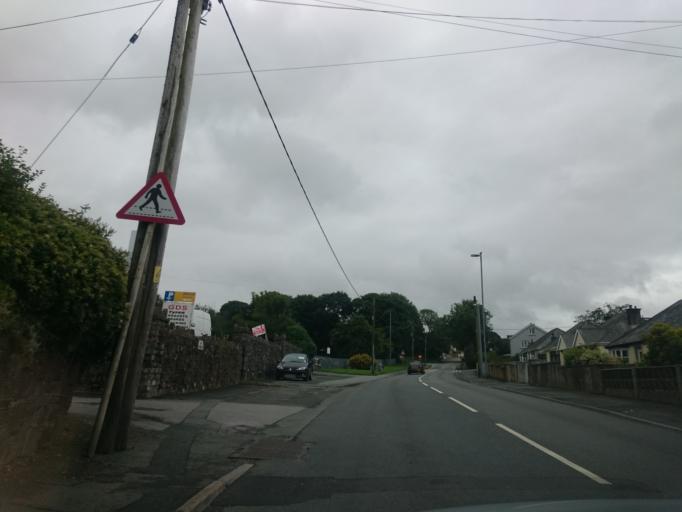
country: GB
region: Wales
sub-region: Pembrokeshire
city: Haverfordwest
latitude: 51.7902
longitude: -4.9763
